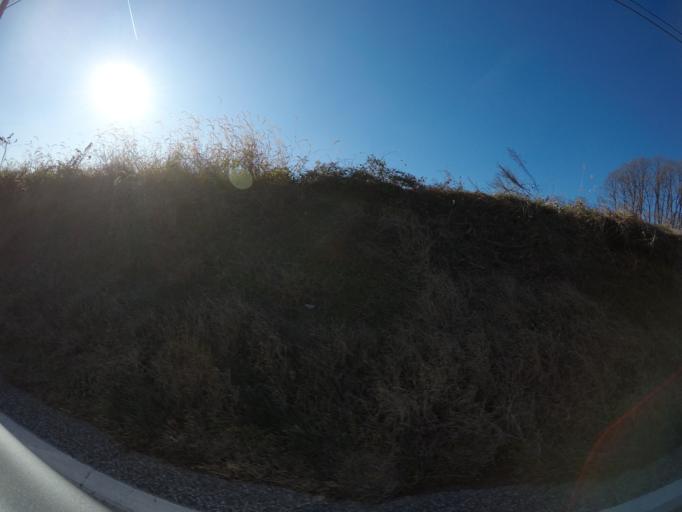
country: US
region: Maryland
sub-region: Harford County
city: South Bel Air
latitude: 39.5819
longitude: -76.2586
